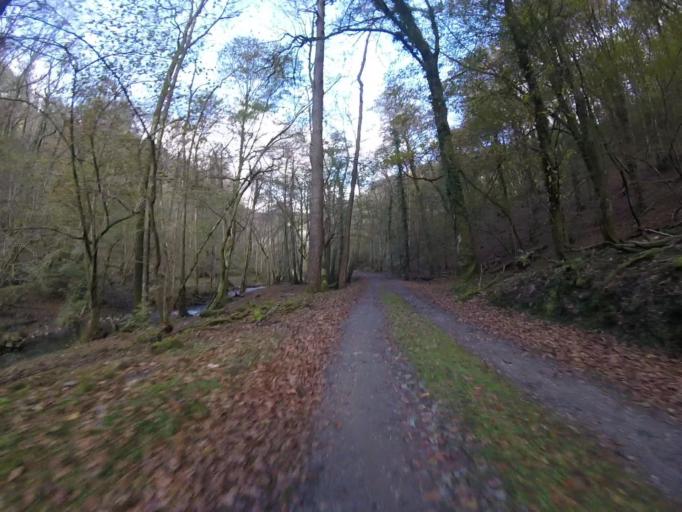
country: ES
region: Navarre
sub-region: Provincia de Navarra
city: Goizueta
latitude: 43.2067
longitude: -1.8124
